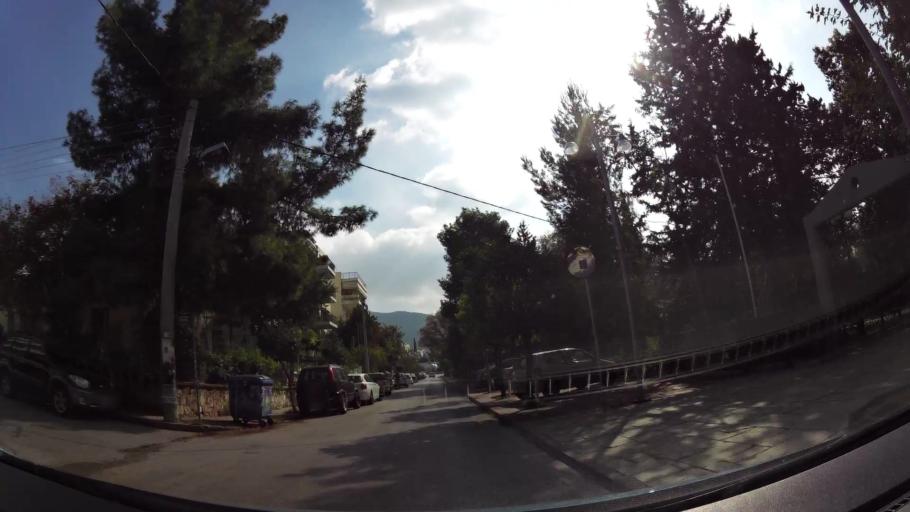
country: GR
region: Attica
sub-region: Nomarchia Athinas
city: Papagou
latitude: 37.9932
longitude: 23.7962
